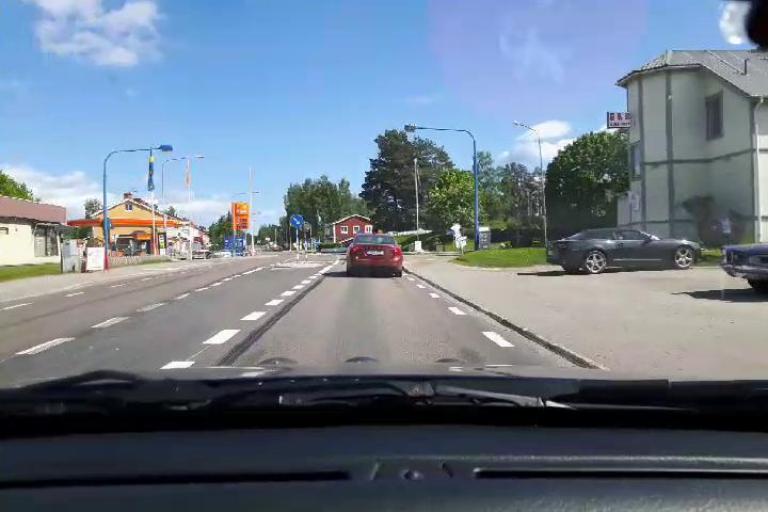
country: SE
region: Gaevleborg
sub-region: Hudiksvalls Kommun
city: Delsbo
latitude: 61.7986
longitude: 16.5505
